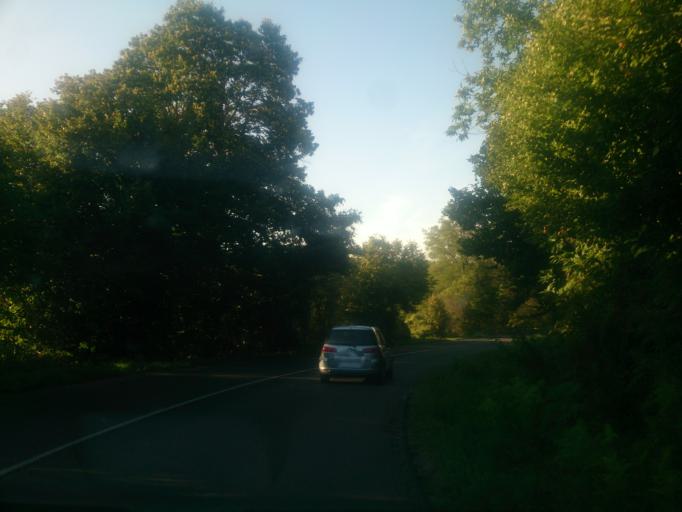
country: FR
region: Limousin
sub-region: Departement de la Correze
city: Brive-la-Gaillarde
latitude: 45.1439
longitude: 1.5266
